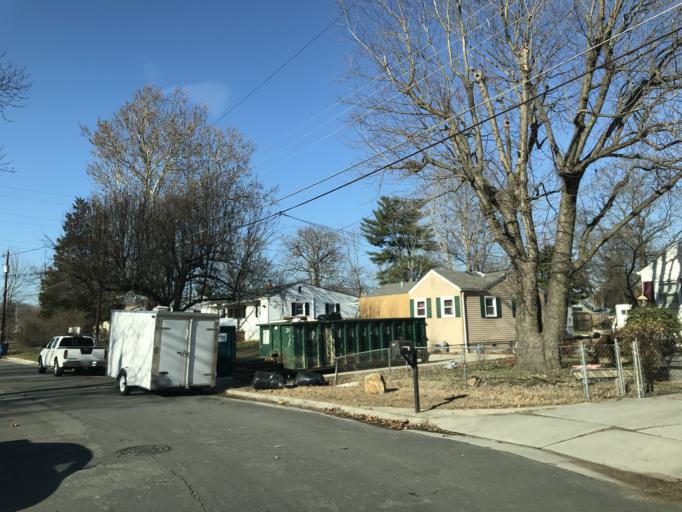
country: US
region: Virginia
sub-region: Fairfax County
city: Franconia
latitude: 38.7769
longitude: -77.1552
